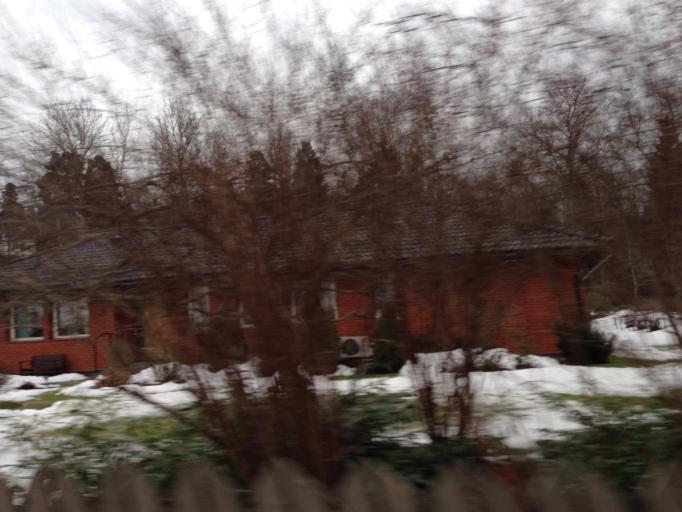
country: SE
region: Stockholm
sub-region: Salems Kommun
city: Ronninge
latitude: 59.1927
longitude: 17.7372
